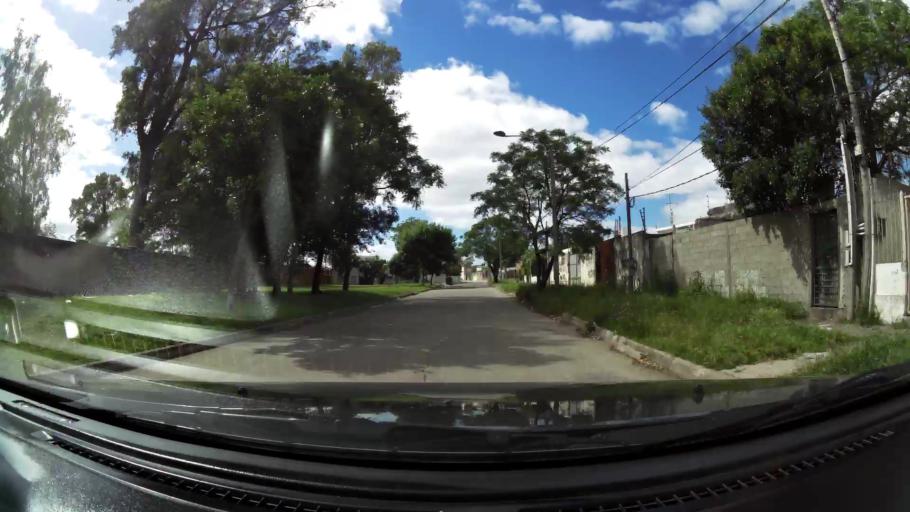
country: UY
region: Montevideo
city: Montevideo
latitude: -34.8783
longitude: -56.1379
